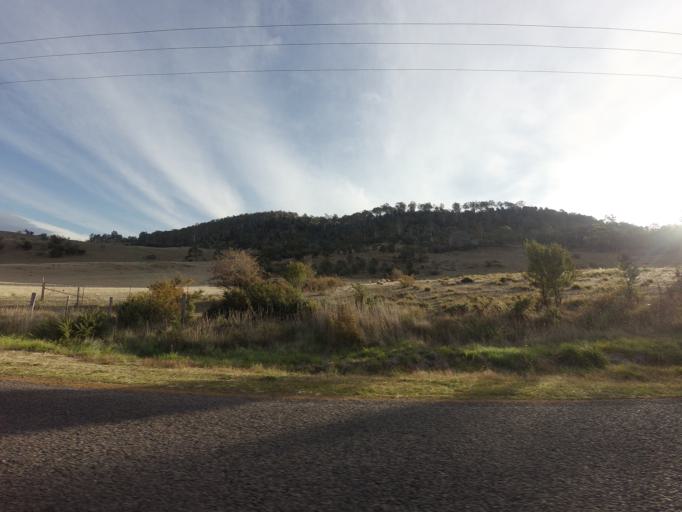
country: AU
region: Tasmania
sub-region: Brighton
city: Bridgewater
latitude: -42.4296
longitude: 147.1425
